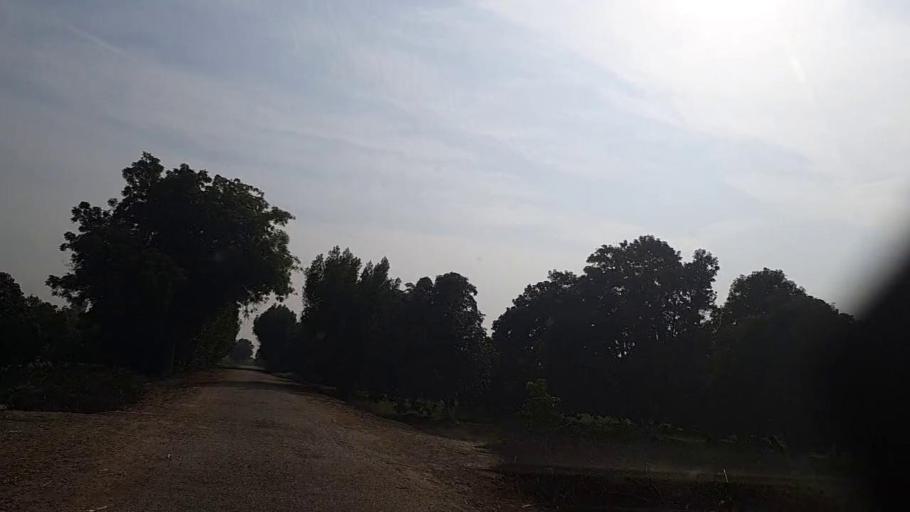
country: PK
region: Sindh
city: Daur
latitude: 26.4017
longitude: 68.2133
